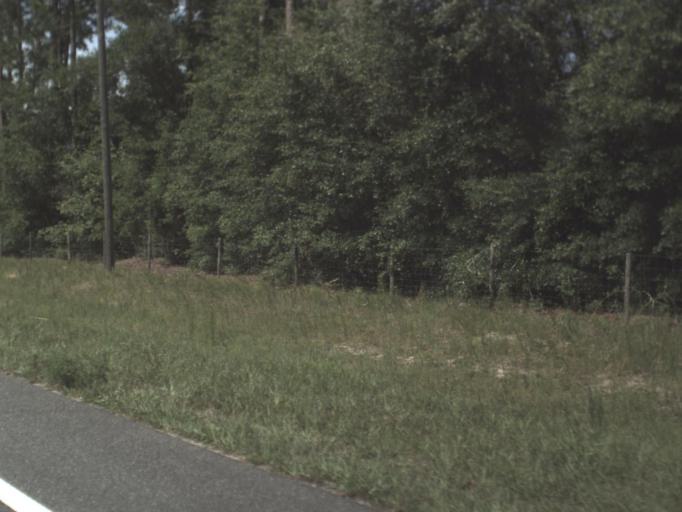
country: US
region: Florida
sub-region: Alachua County
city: High Springs
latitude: 29.8560
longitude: -82.7420
